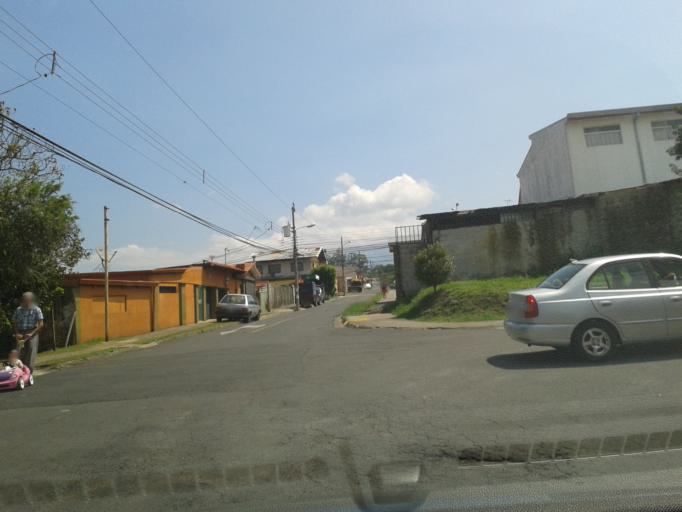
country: CR
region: Heredia
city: San Francisco
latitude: 9.9861
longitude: -84.1361
